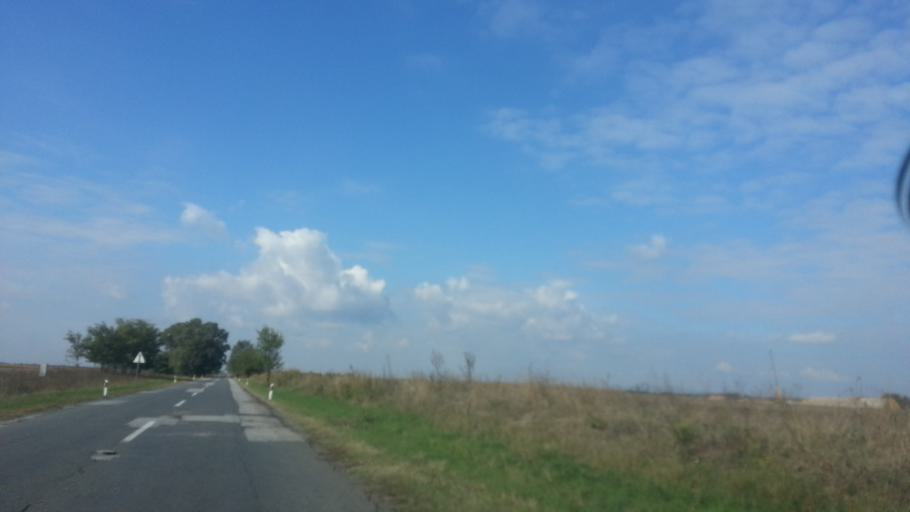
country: RS
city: Stari Banovci
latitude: 44.9864
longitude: 20.2427
